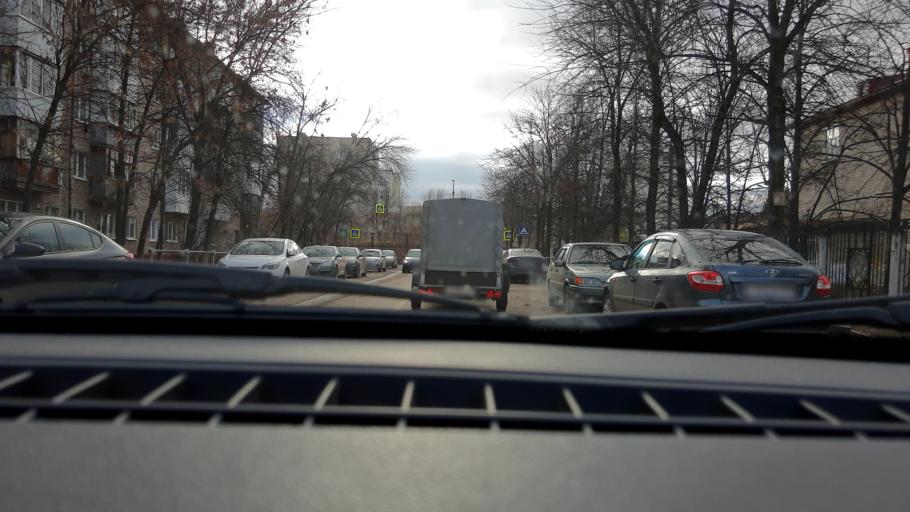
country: RU
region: Bashkortostan
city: Ufa
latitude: 54.7788
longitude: 56.0268
